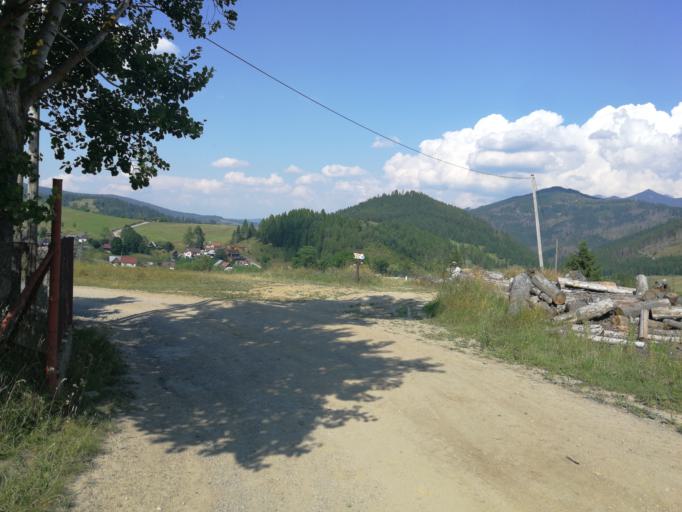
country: SK
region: Zilinsky
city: Tvrdosin
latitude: 49.1935
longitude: 19.5151
